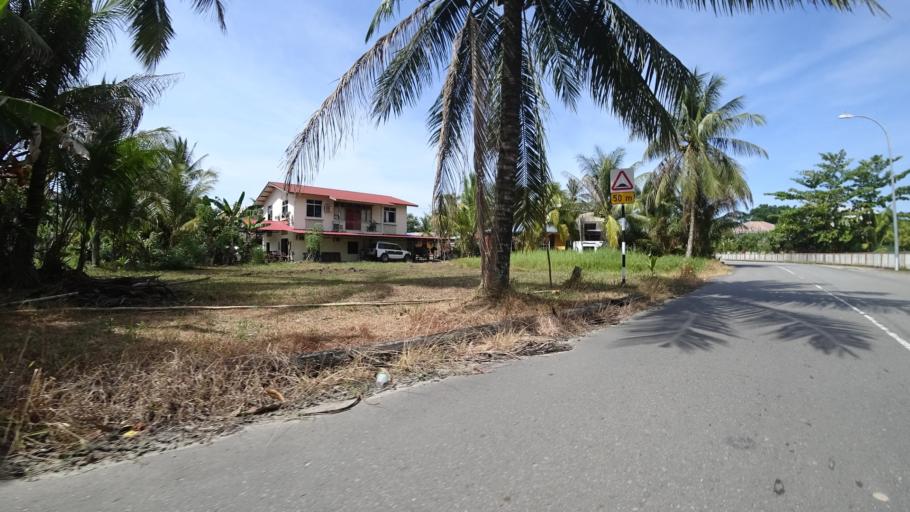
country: BN
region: Brunei and Muara
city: Bandar Seri Begawan
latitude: 4.8917
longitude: 114.8491
